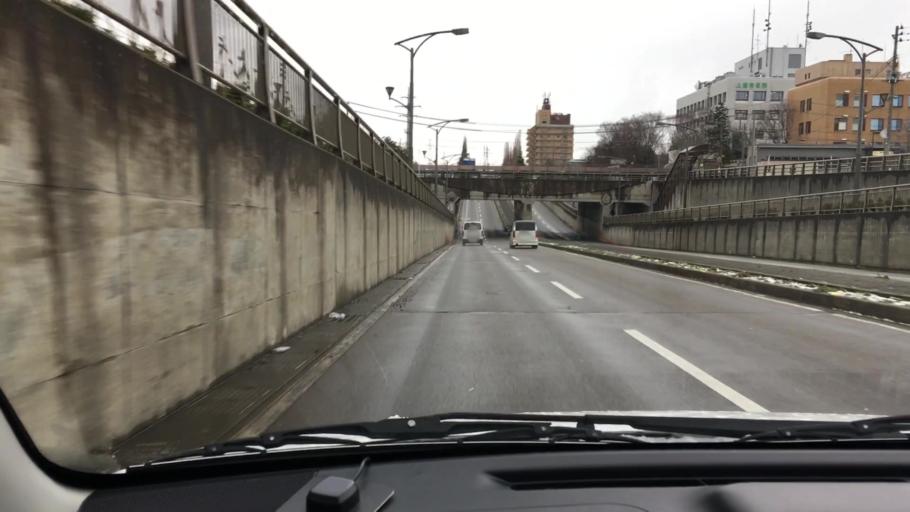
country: JP
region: Niigata
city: Joetsu
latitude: 37.1483
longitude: 138.2336
